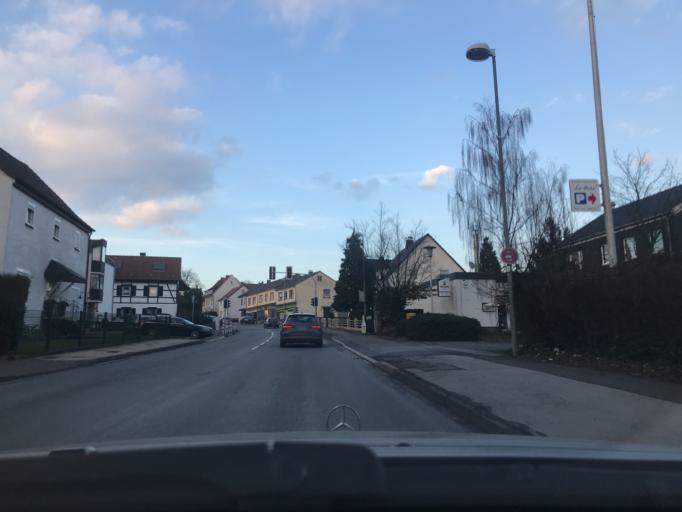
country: DE
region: North Rhine-Westphalia
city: Wickede
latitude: 51.4966
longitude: 7.8700
